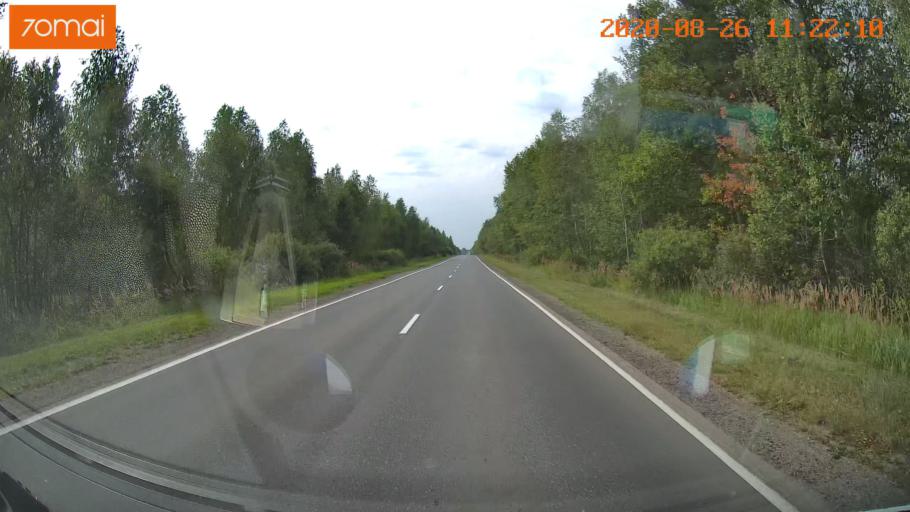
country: RU
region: Rjazan
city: Shilovo
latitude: 54.3673
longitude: 41.0320
